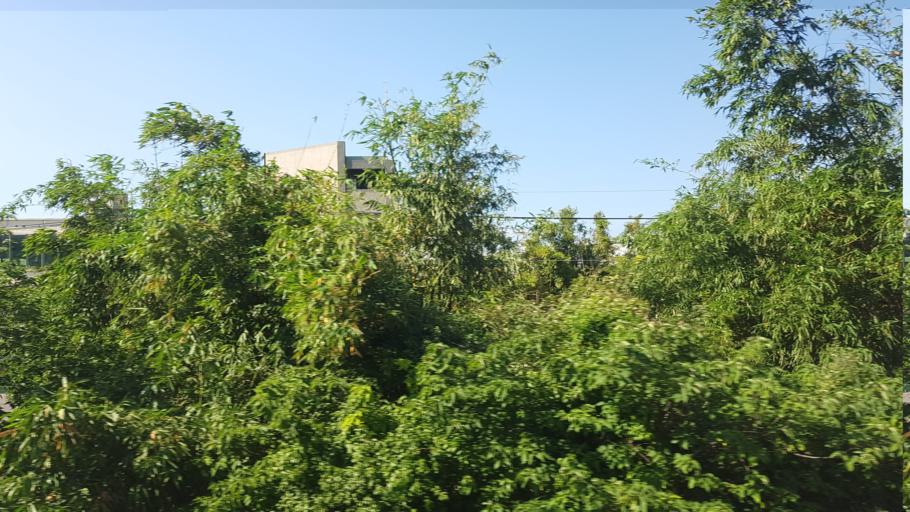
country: TW
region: Taiwan
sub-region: Hsinchu
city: Hsinchu
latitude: 24.7379
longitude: 120.8930
